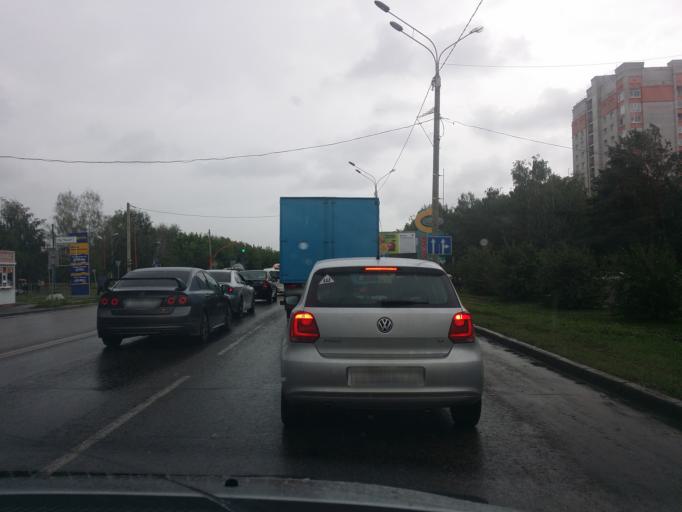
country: RU
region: Altai Krai
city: Novosilikatnyy
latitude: 53.3450
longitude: 83.6659
